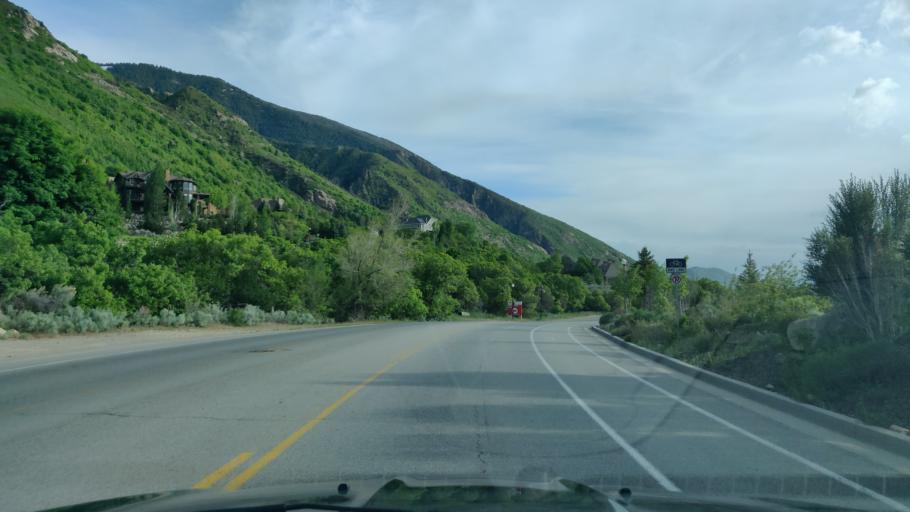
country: US
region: Utah
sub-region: Salt Lake County
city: Granite
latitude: 40.5520
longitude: -111.8027
